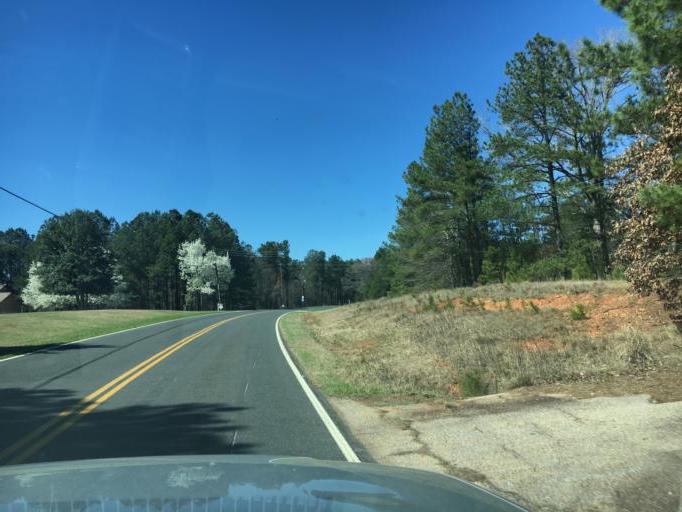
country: US
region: South Carolina
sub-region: Greenwood County
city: Ninety Six
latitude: 34.2936
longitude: -81.9723
